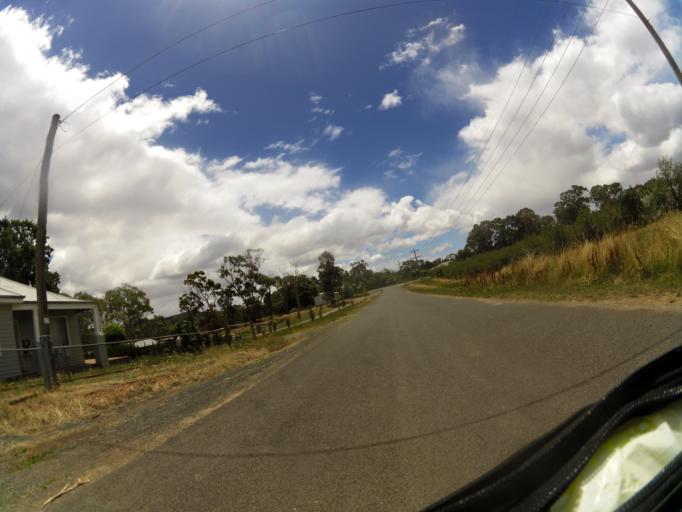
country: AU
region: Victoria
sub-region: Mount Alexander
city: Castlemaine
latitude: -37.0175
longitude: 144.2523
